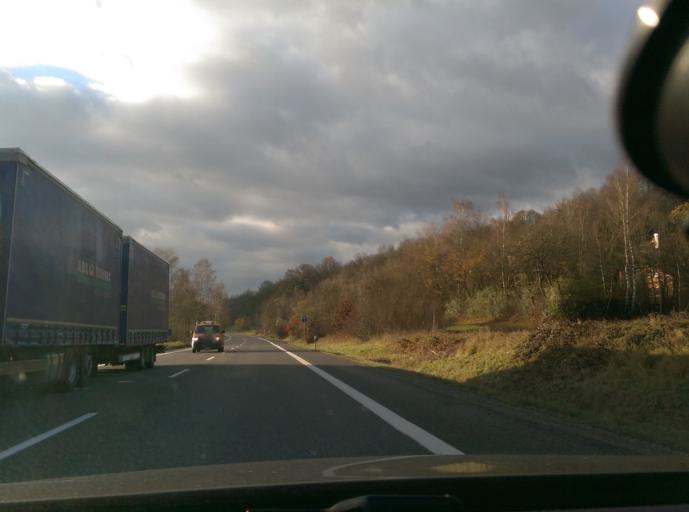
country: DE
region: Hesse
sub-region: Regierungsbezirk Kassel
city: Eschwege
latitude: 51.2041
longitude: 9.9987
